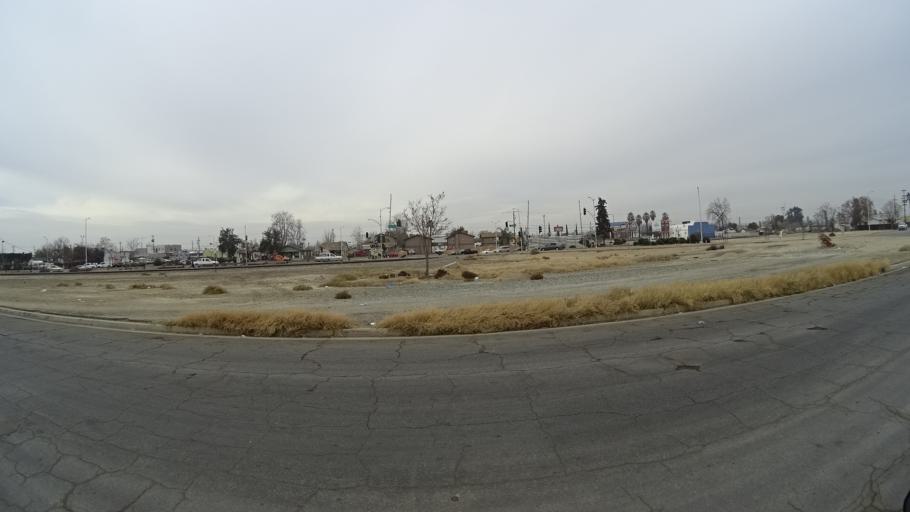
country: US
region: California
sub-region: Kern County
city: Bakersfield
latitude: 35.3731
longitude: -118.9916
